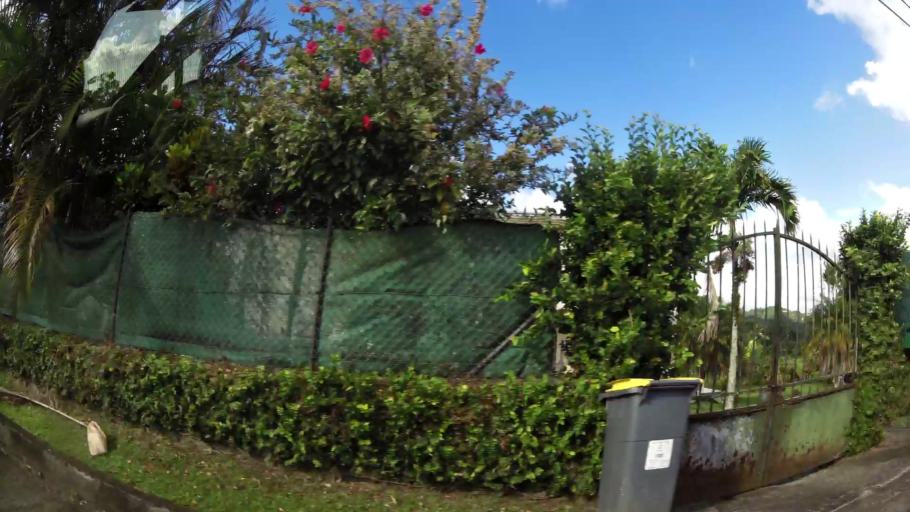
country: MQ
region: Martinique
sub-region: Martinique
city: Fort-de-France
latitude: 14.6498
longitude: -61.0837
